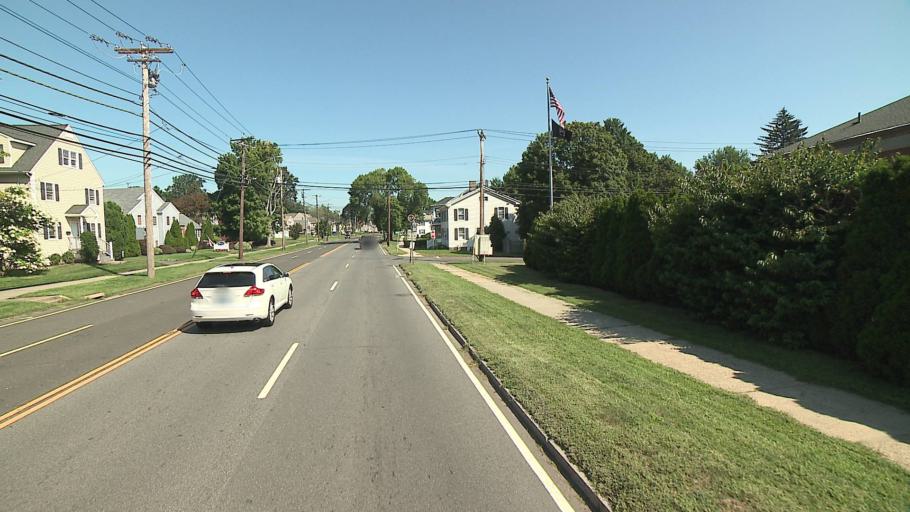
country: US
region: Connecticut
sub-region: Fairfield County
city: Stratford
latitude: 41.2028
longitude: -73.1313
